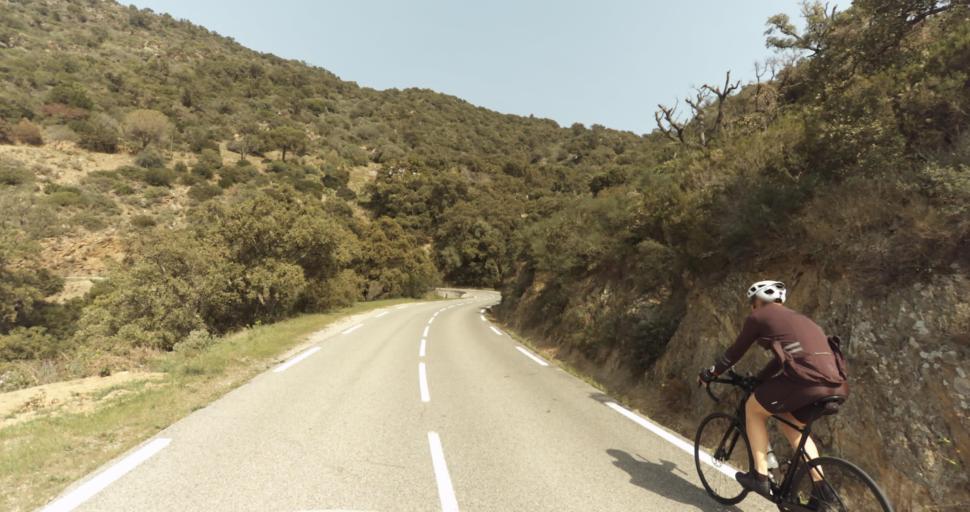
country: FR
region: Provence-Alpes-Cote d'Azur
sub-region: Departement du Var
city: Bormes-les-Mimosas
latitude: 43.1630
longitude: 6.3439
